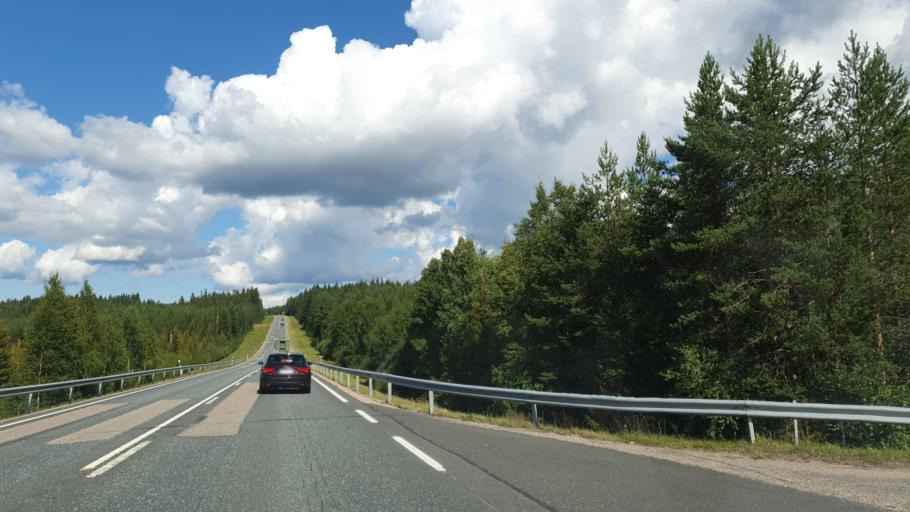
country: FI
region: Kainuu
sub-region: Kajaani
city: Kajaani
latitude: 64.0840
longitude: 27.4529
